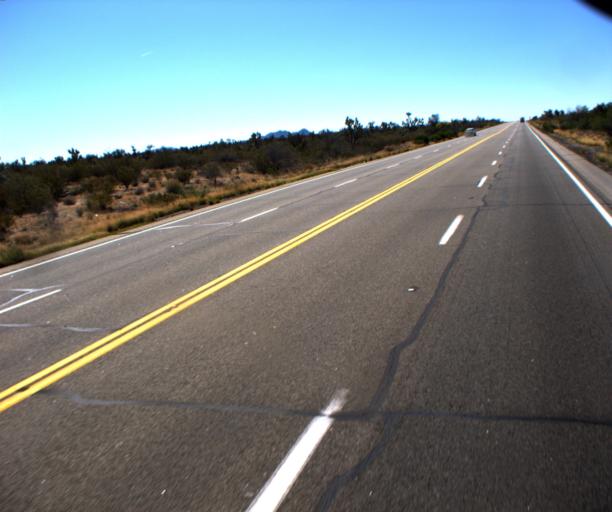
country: US
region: Arizona
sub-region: Yavapai County
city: Congress
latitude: 34.2825
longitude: -113.1041
